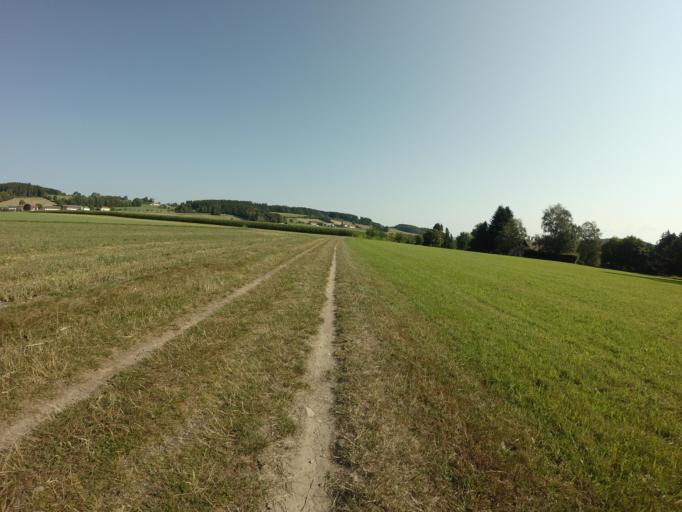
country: AT
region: Upper Austria
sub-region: Politischer Bezirk Urfahr-Umgebung
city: Bad Leonfelden
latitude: 48.5390
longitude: 14.3141
